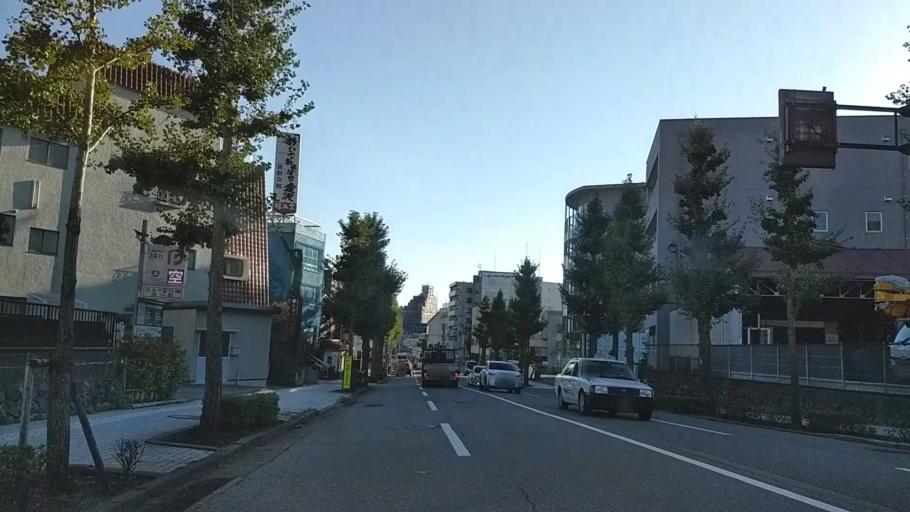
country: JP
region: Ishikawa
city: Nonoichi
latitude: 36.5573
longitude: 136.6590
